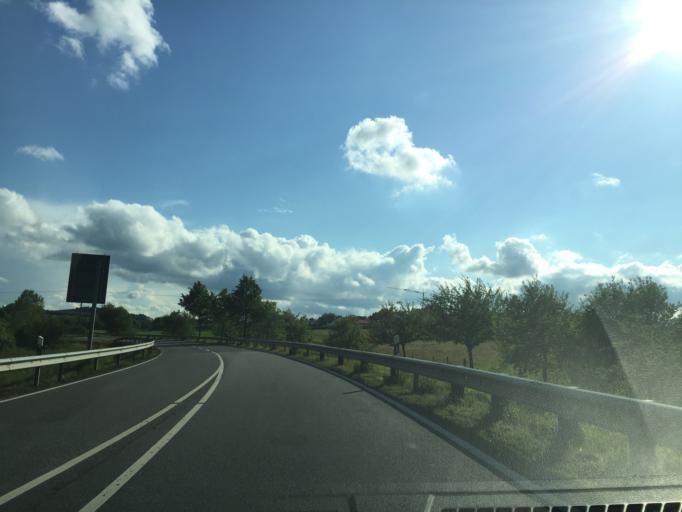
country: DE
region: Rheinland-Pfalz
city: Meudt
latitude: 50.4979
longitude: 7.9069
